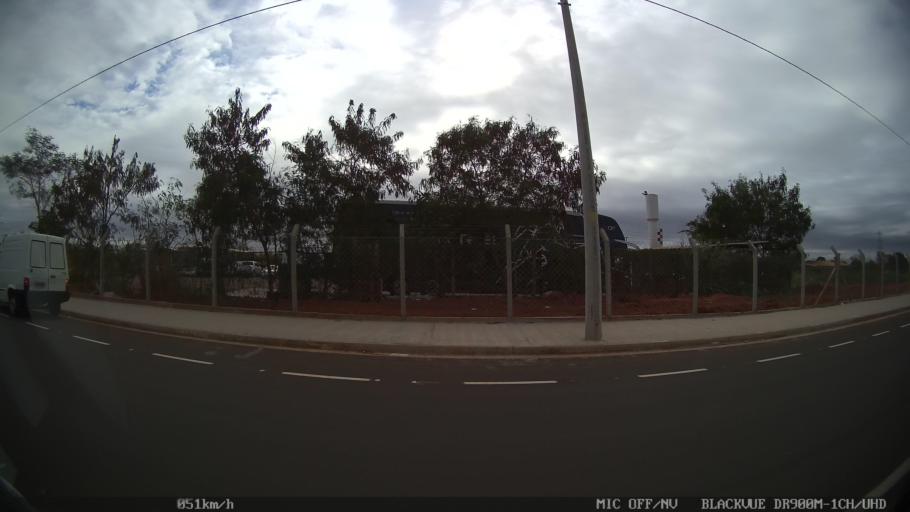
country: BR
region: Sao Paulo
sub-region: Sao Jose Do Rio Preto
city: Sao Jose do Rio Preto
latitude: -20.8269
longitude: -49.4155
